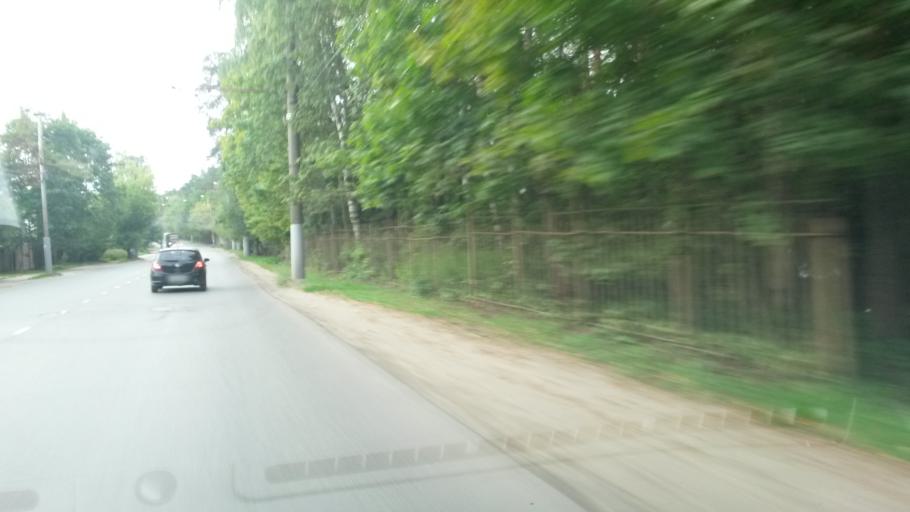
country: RU
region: Ivanovo
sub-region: Gorod Ivanovo
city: Ivanovo
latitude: 57.0241
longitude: 40.9429
